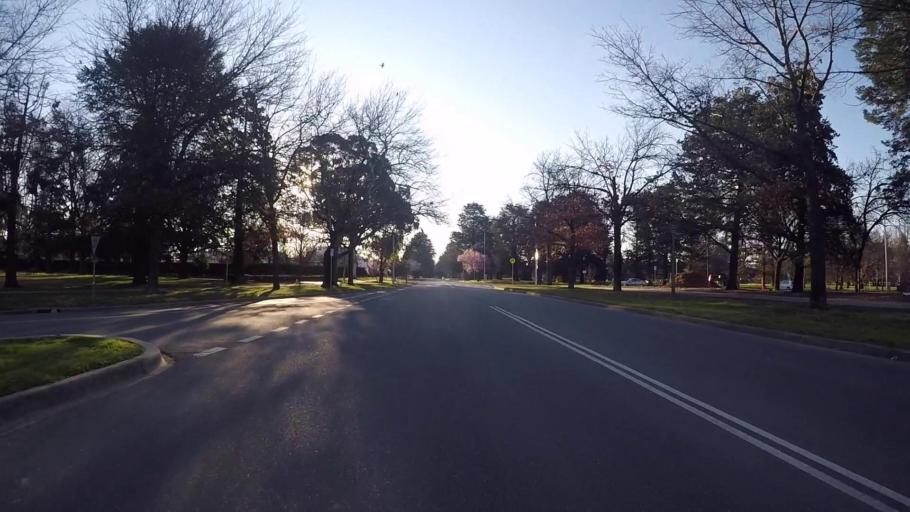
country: AU
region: Australian Capital Territory
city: Forrest
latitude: -35.3033
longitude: 149.1330
